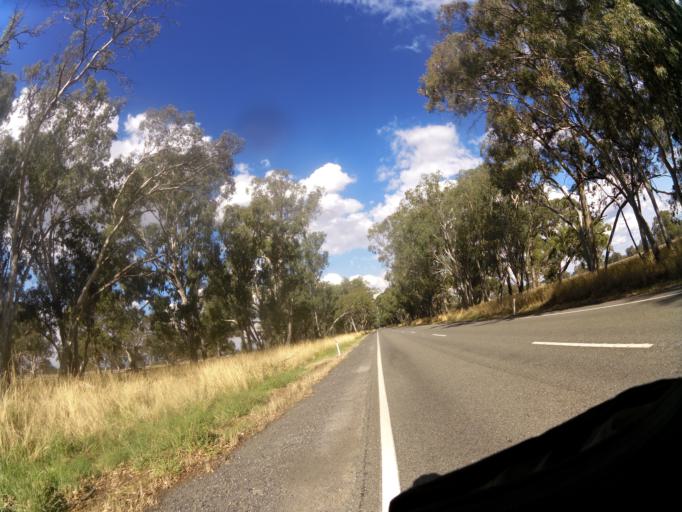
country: AU
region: Victoria
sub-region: Mansfield
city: Mansfield
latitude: -36.9990
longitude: 146.0665
